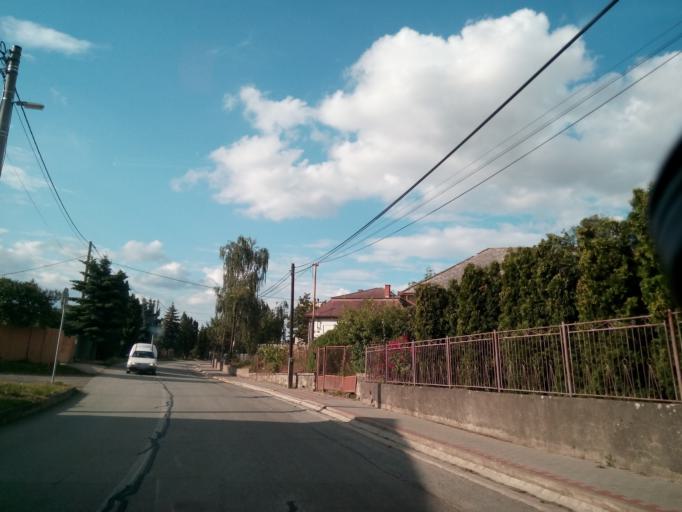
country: SK
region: Kosicky
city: Secovce
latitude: 48.6010
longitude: 21.5581
